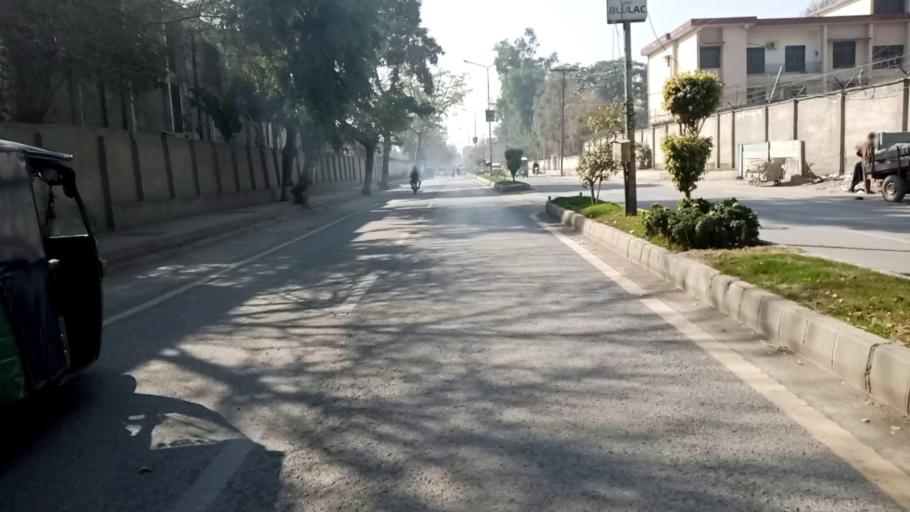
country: PK
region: Khyber Pakhtunkhwa
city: Peshawar
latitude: 33.9888
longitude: 71.5318
